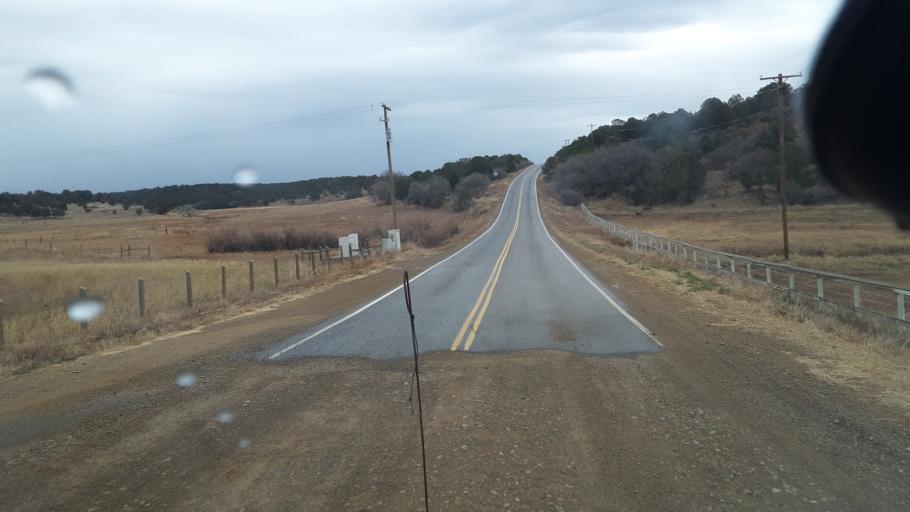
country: US
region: Colorado
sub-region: Montezuma County
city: Mancos
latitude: 37.1984
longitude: -108.1239
